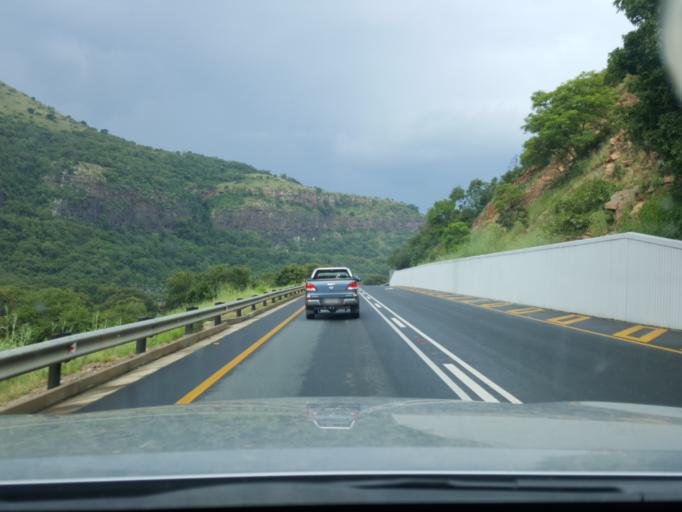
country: ZA
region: Mpumalanga
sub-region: Nkangala District Municipality
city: Belfast
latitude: -25.6464
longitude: 30.3667
